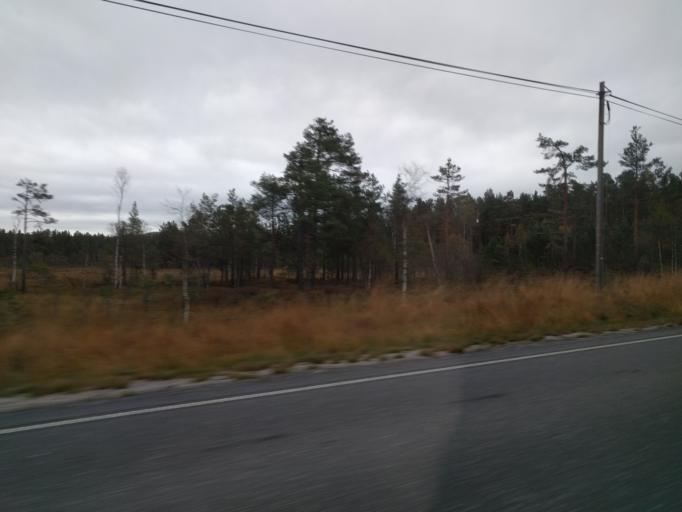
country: NO
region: Aust-Agder
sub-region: Evje og Hornnes
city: Evje
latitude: 58.5123
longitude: 7.7675
